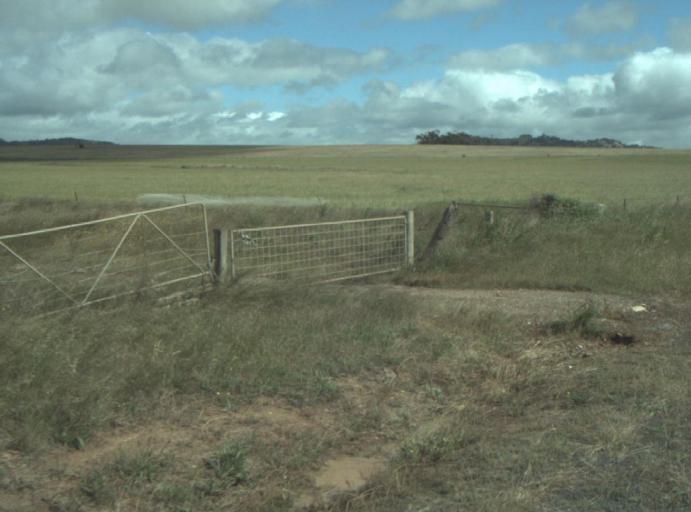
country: AU
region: Victoria
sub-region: Greater Geelong
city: Lara
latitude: -37.9008
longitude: 144.3175
